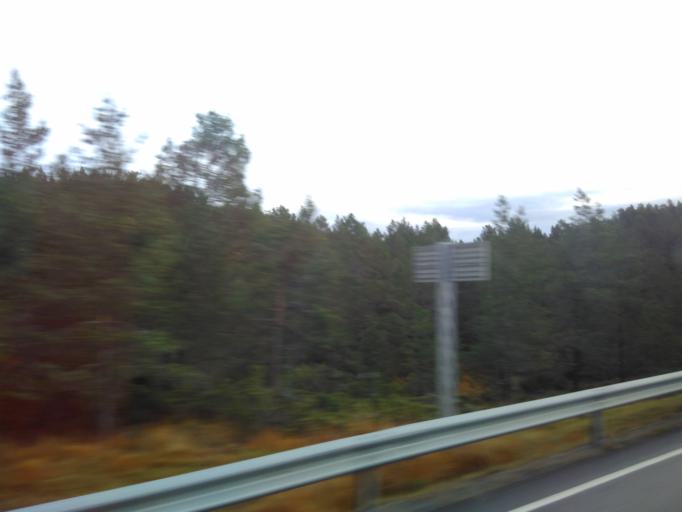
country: NO
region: Sor-Trondelag
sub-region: Hitra
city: Fillan
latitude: 63.5719
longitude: 9.0297
